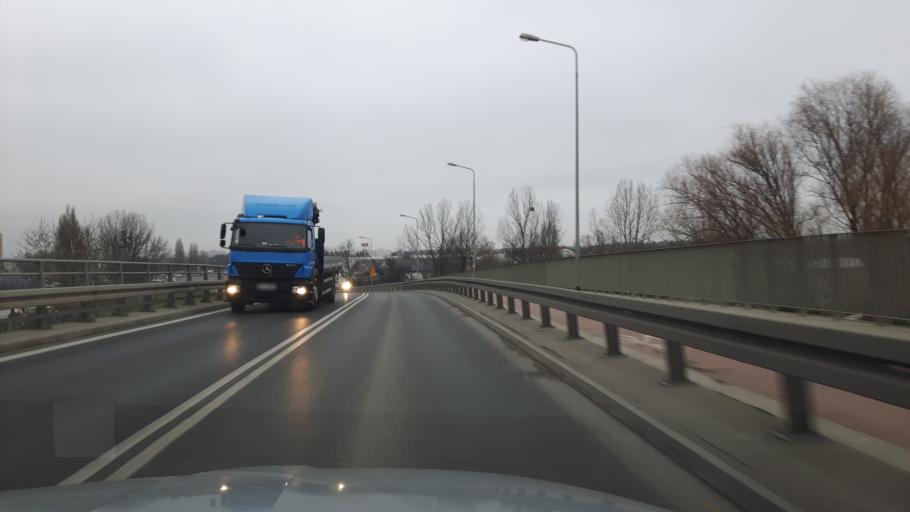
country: PL
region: Masovian Voivodeship
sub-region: Warszawa
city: Targowek
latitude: 52.2712
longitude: 21.0699
